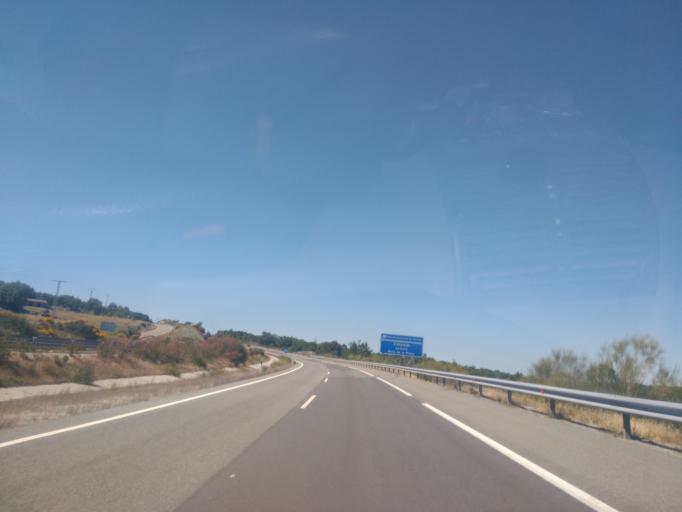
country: ES
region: Castille and Leon
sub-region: Provincia de Salamanca
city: Nava de Bejar
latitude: 40.4640
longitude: -5.6776
